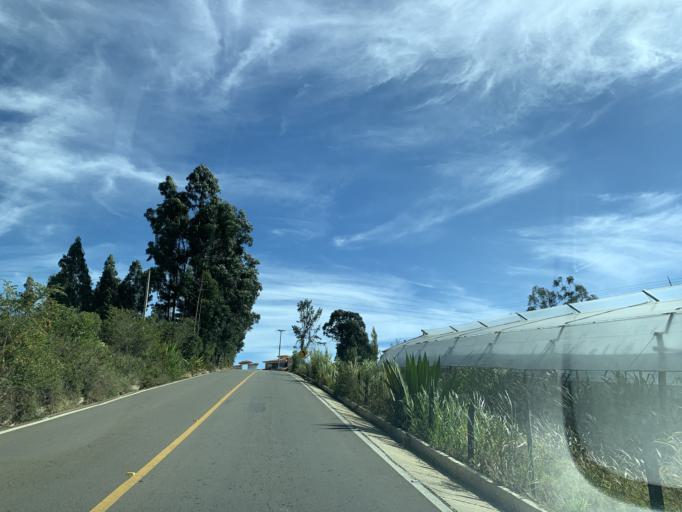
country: CO
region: Boyaca
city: Santa Sofia
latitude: 5.6924
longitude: -73.5890
